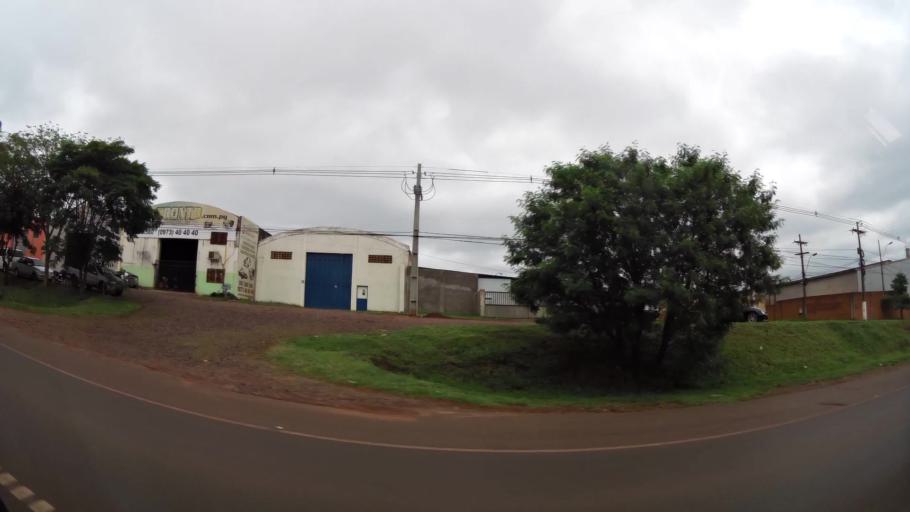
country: PY
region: Alto Parana
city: Ciudad del Este
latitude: -25.4941
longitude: -54.7115
